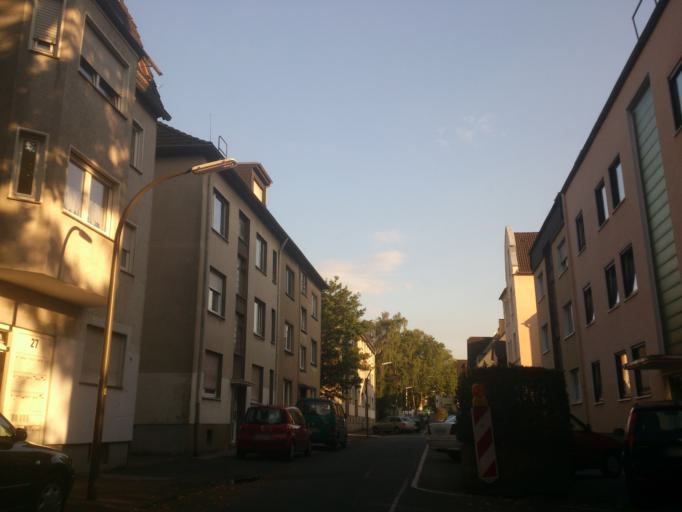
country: DE
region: North Rhine-Westphalia
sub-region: Regierungsbezirk Arnsberg
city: Dortmund
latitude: 51.4841
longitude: 7.4358
